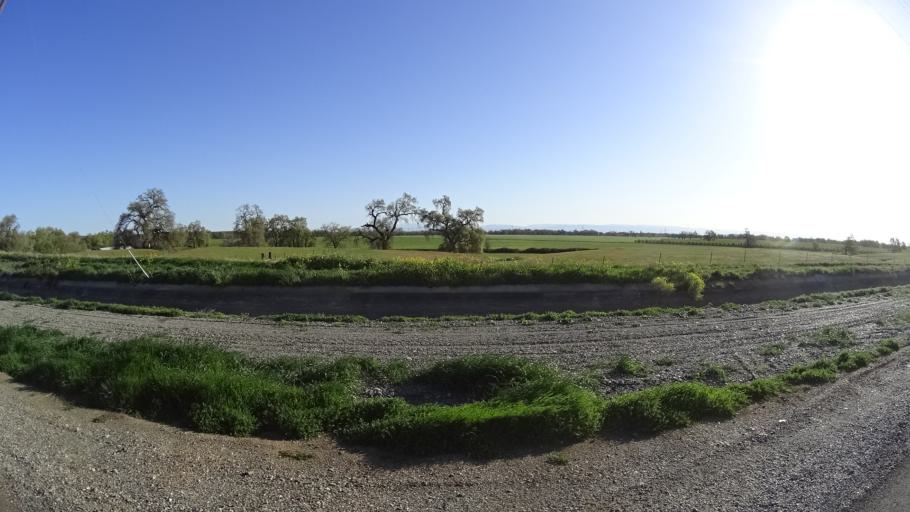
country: US
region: California
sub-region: Glenn County
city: Orland
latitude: 39.7859
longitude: -122.3007
